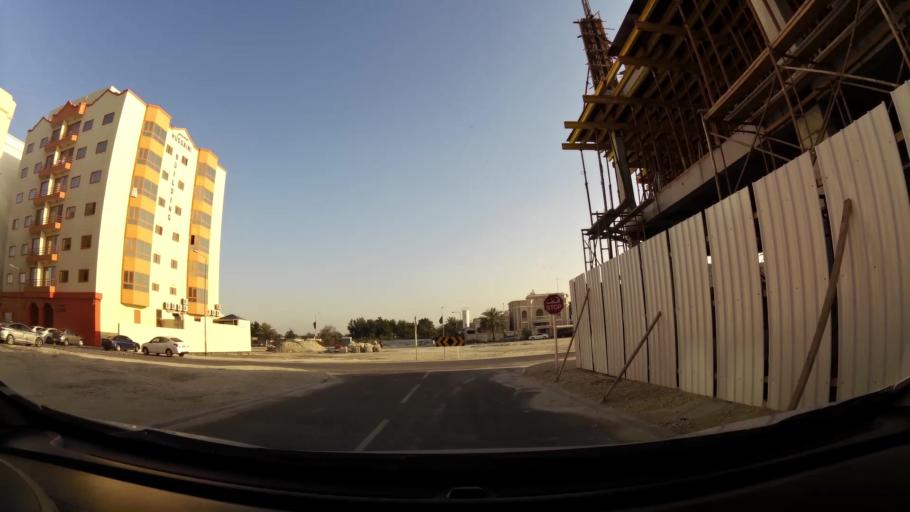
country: BH
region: Manama
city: Jidd Hafs
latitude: 26.2254
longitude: 50.5547
